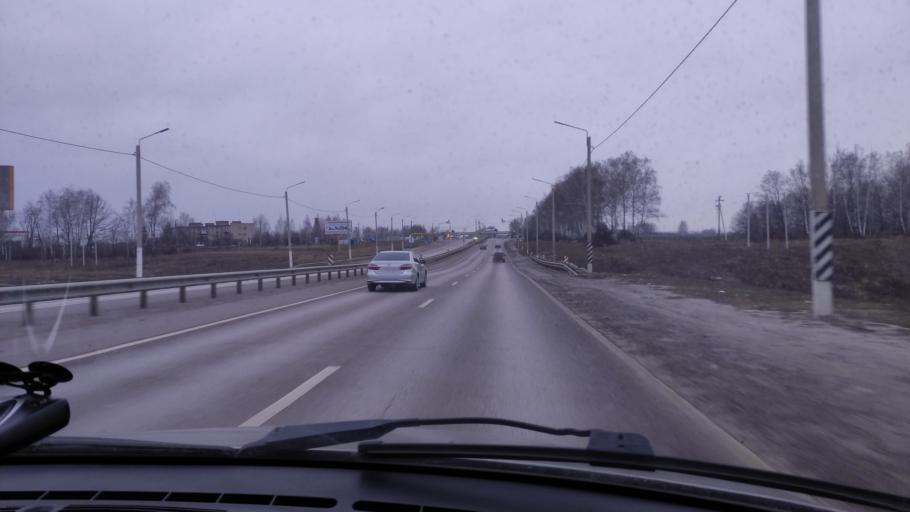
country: RU
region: Tambov
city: Komsomolets
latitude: 52.7321
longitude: 41.3060
